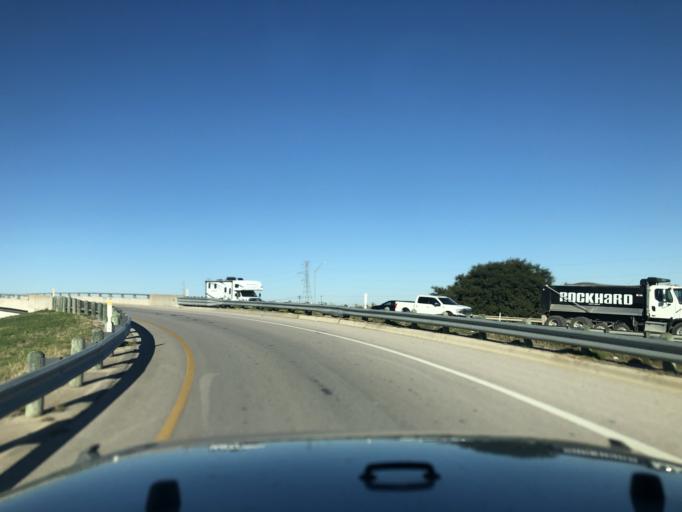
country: US
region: Texas
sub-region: Williamson County
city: Georgetown
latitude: 30.5768
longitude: -97.6923
